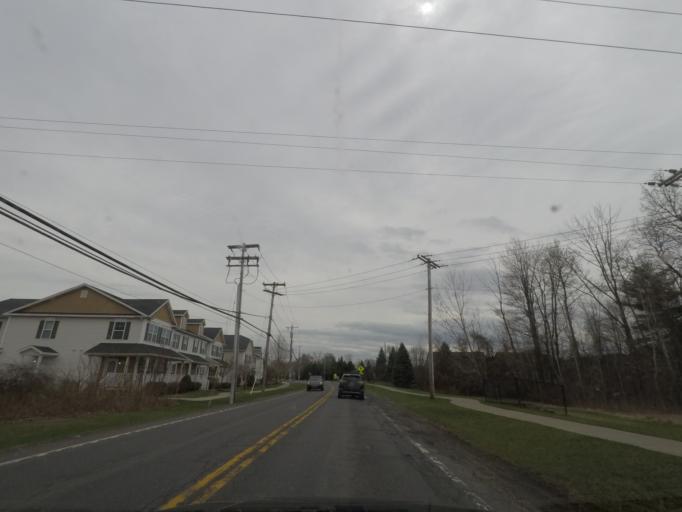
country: US
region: New York
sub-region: Albany County
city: Delmar
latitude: 42.6044
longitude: -73.8184
